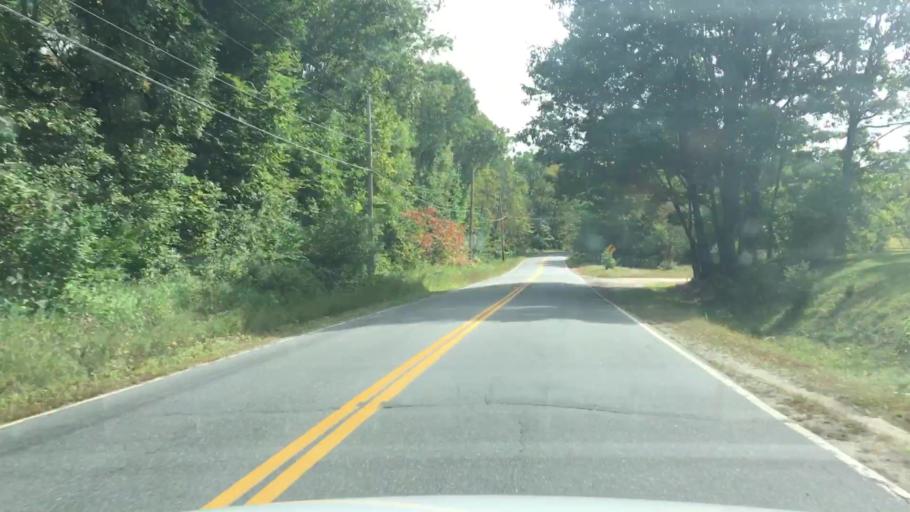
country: US
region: Maine
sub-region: Androscoggin County
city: Lewiston
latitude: 44.0325
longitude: -70.1851
